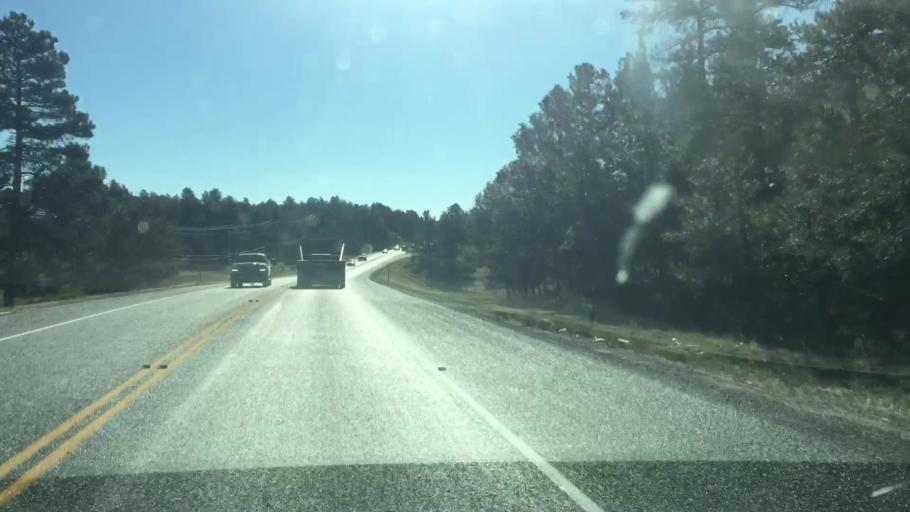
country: US
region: Colorado
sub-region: Douglas County
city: The Pinery
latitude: 39.3840
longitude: -104.7276
